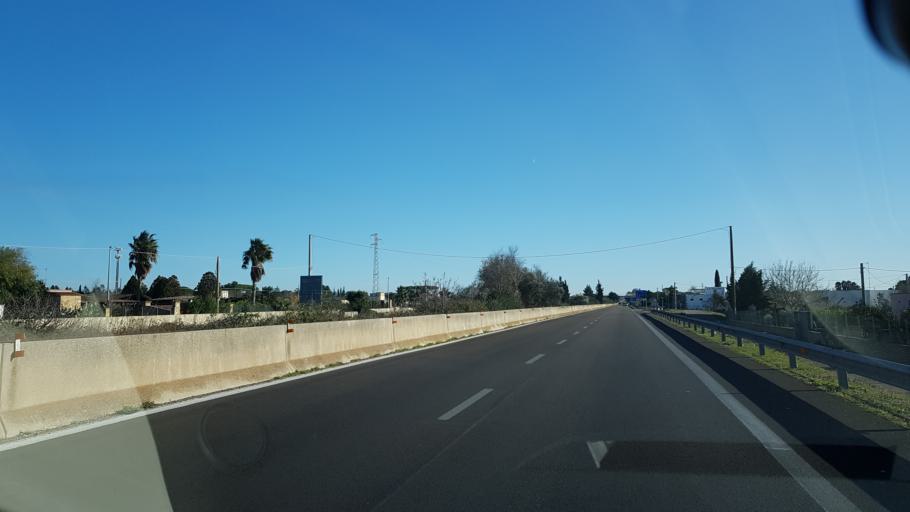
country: IT
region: Apulia
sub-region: Provincia di Lecce
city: Gallipoli
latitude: 40.0379
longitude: 18.0230
